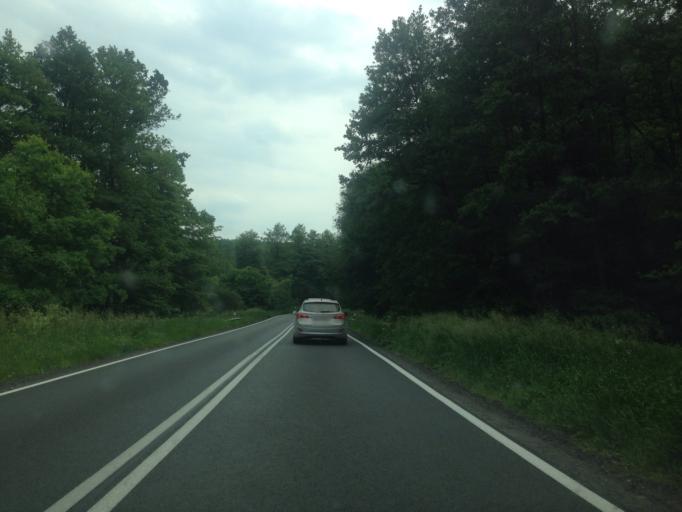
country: PL
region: Kujawsko-Pomorskie
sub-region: Powiat grudziadzki
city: Rogozno
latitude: 53.5082
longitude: 18.9256
